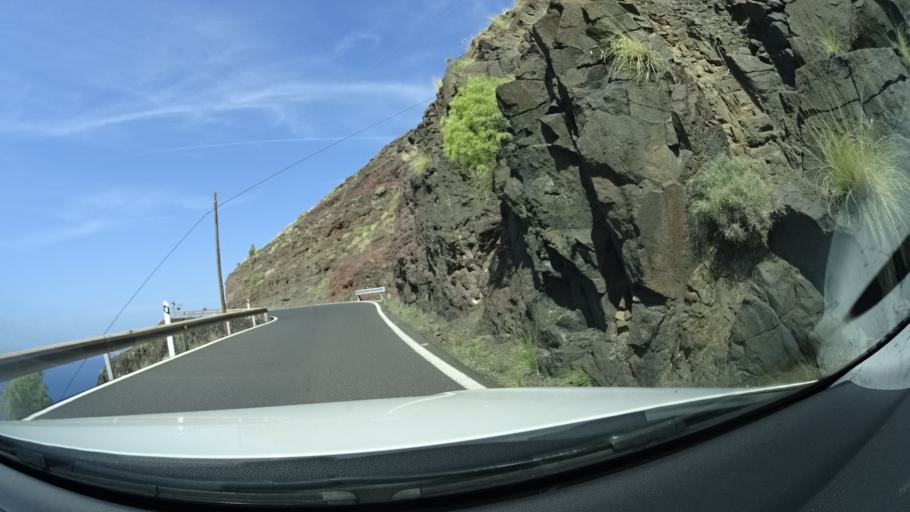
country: ES
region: Canary Islands
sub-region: Provincia de Las Palmas
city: Agaete
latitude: 28.0901
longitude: -15.7045
